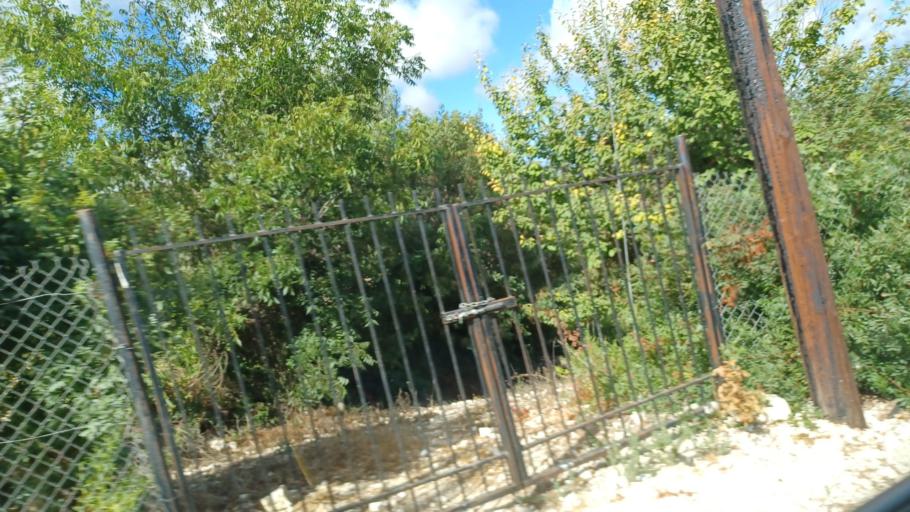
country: CY
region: Pafos
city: Tala
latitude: 34.8606
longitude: 32.4515
